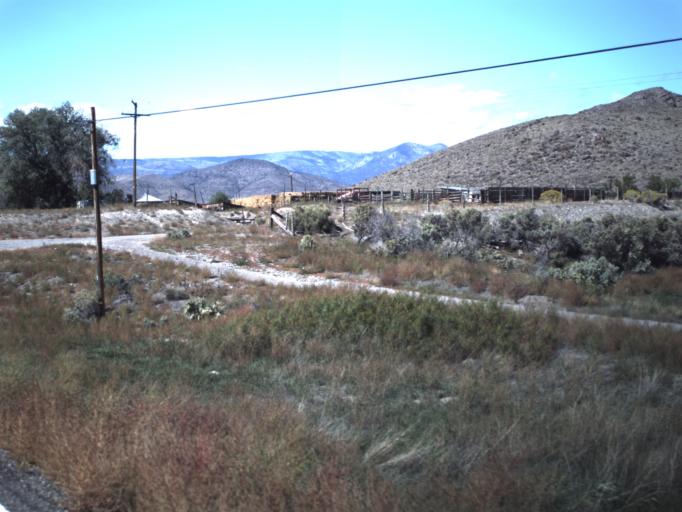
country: US
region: Utah
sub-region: Piute County
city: Junction
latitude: 38.2084
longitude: -112.1960
